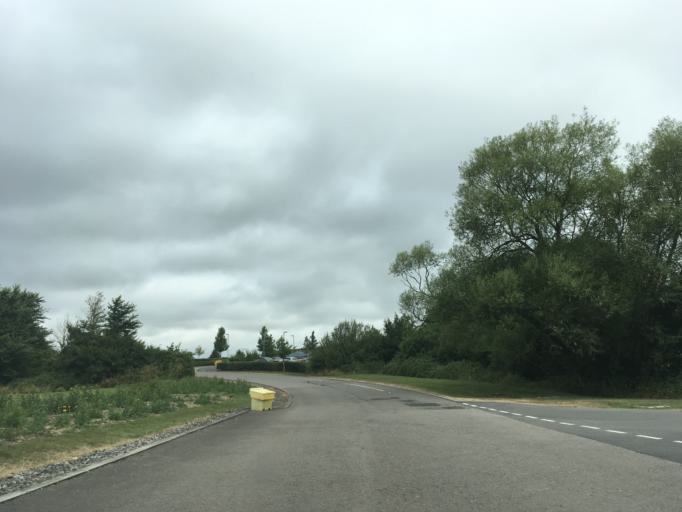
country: GB
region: England
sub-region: South Gloucestershire
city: Charfield
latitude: 51.6329
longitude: -2.3821
